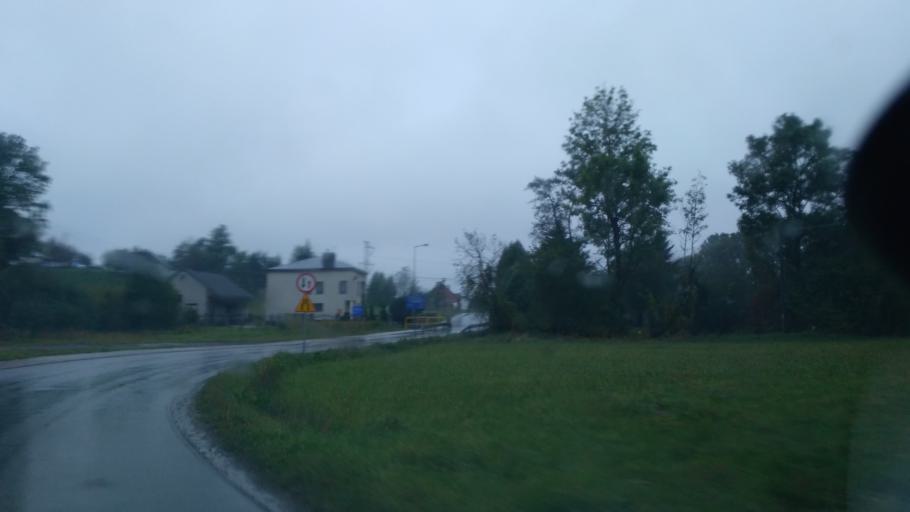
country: PL
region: Subcarpathian Voivodeship
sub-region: Powiat krosnienski
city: Korczyna
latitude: 49.7021
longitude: 21.8125
